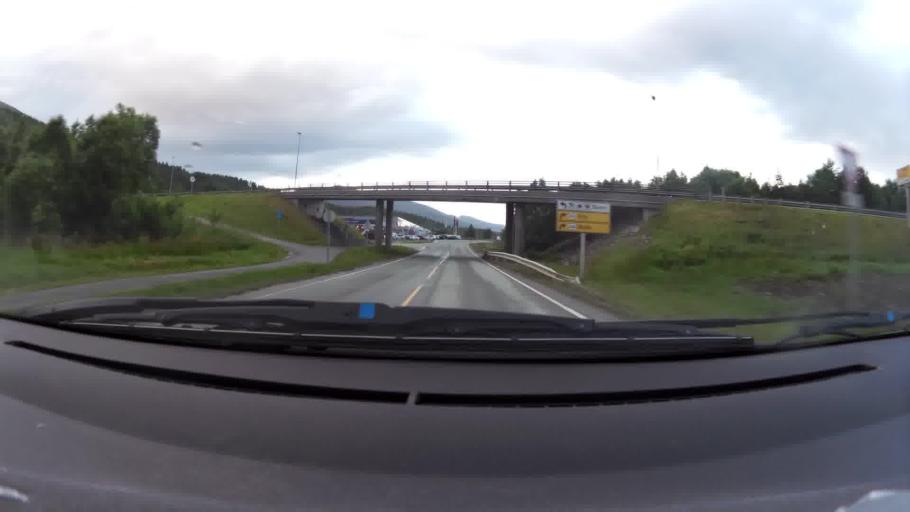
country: NO
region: More og Romsdal
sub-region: Molde
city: Molde
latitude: 62.7658
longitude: 7.2754
